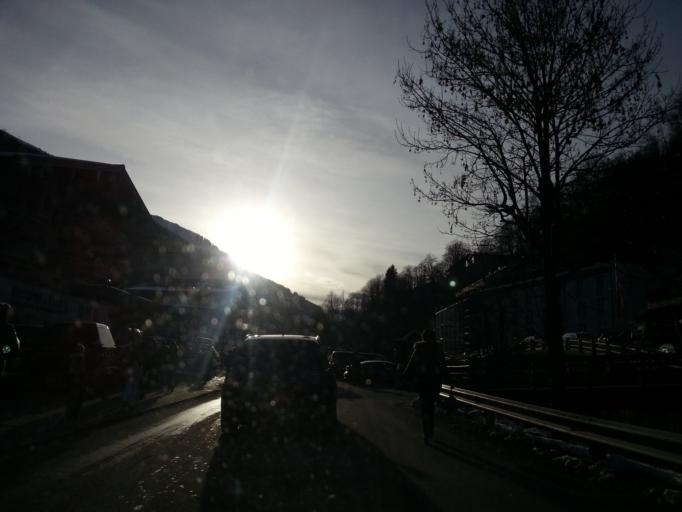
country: AT
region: Salzburg
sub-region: Politischer Bezirk Zell am See
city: Saalbach
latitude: 47.3782
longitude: 12.5930
